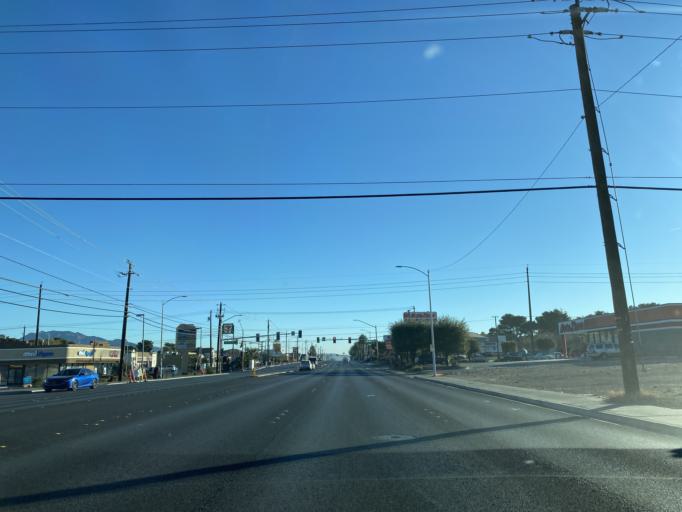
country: US
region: Nevada
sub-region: Clark County
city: Winchester
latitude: 36.1297
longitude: -115.1068
